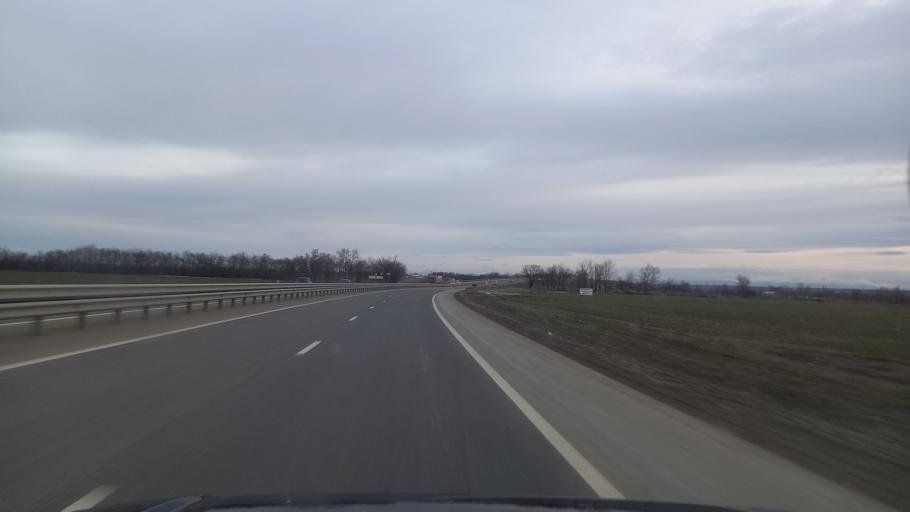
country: RU
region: Adygeya
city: Khanskaya
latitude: 44.7074
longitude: 39.9668
